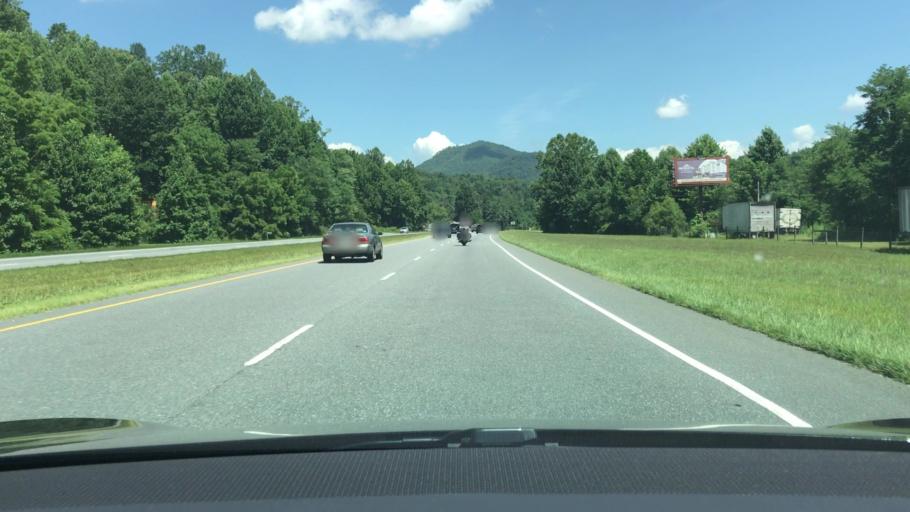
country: US
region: North Carolina
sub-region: Jackson County
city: Sylva
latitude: 35.3139
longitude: -83.2610
